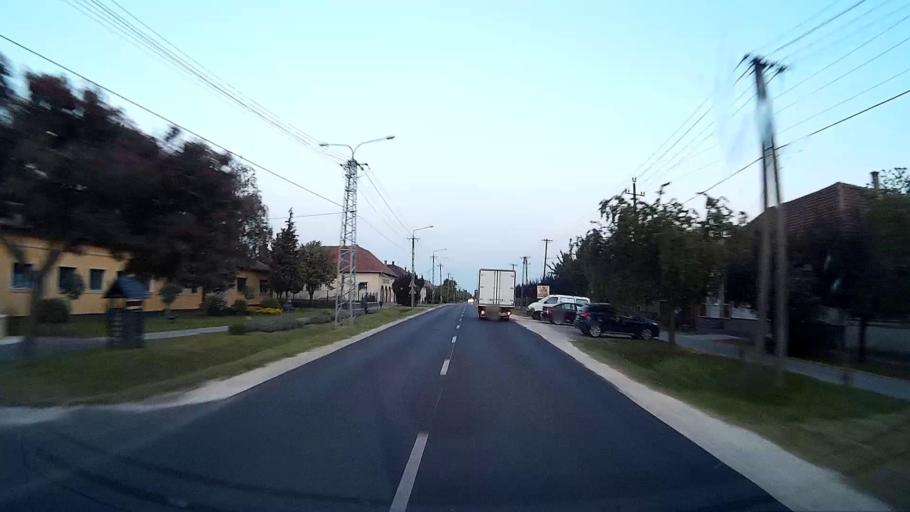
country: HU
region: Pest
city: Cegledbercel
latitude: 47.2158
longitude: 19.6752
